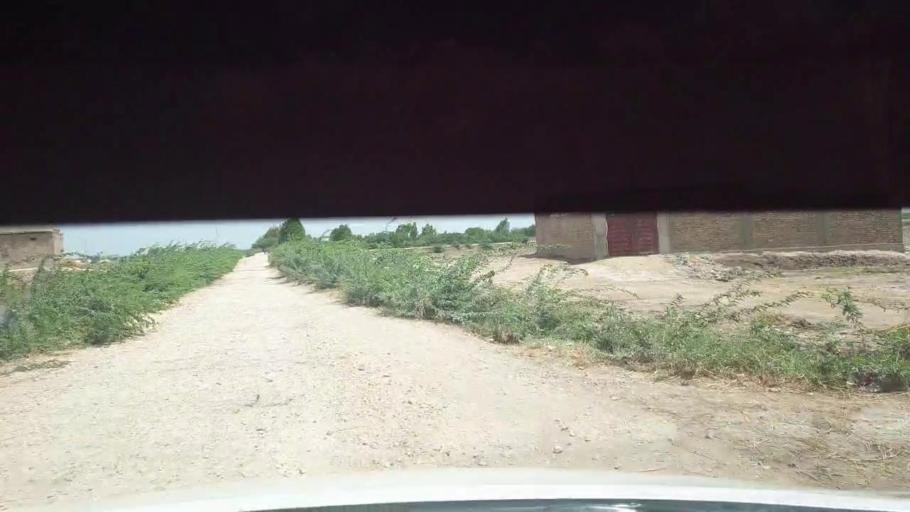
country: PK
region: Sindh
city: Kadhan
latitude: 24.4889
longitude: 68.9832
